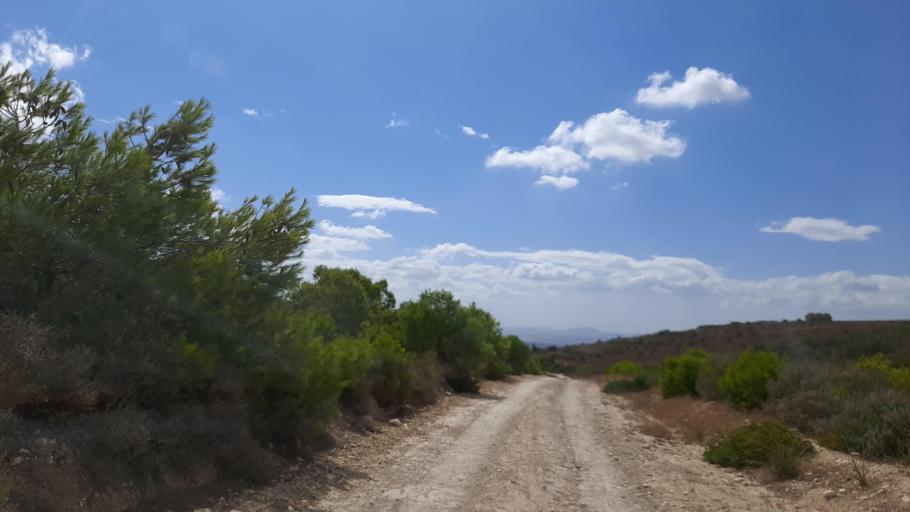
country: TN
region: Zaghwan
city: Zaghouan
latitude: 36.4960
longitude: 10.1736
